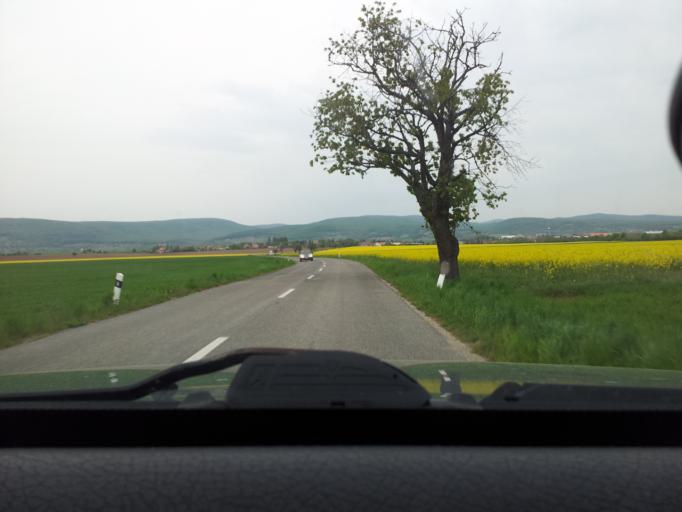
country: SK
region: Nitriansky
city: Tlmace
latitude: 48.2761
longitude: 18.5906
